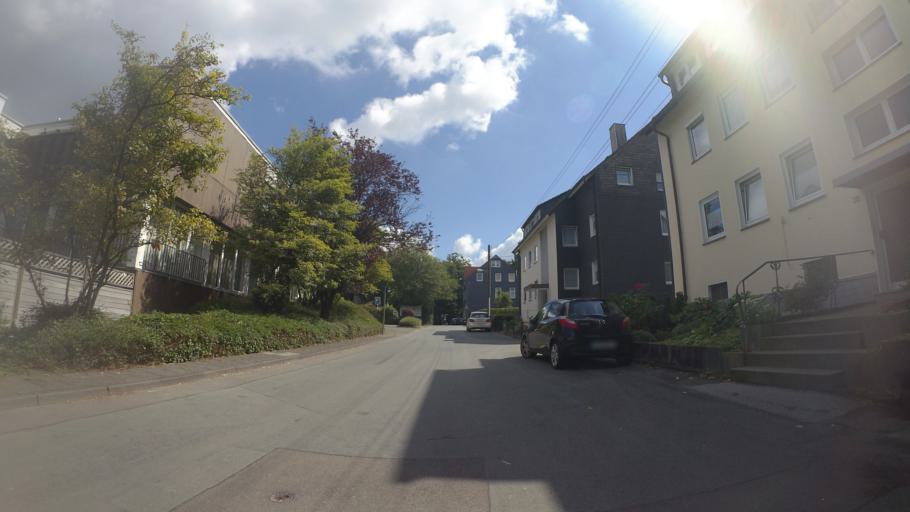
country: DE
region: North Rhine-Westphalia
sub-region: Regierungsbezirk Dusseldorf
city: Remscheid
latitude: 51.2094
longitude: 7.2481
